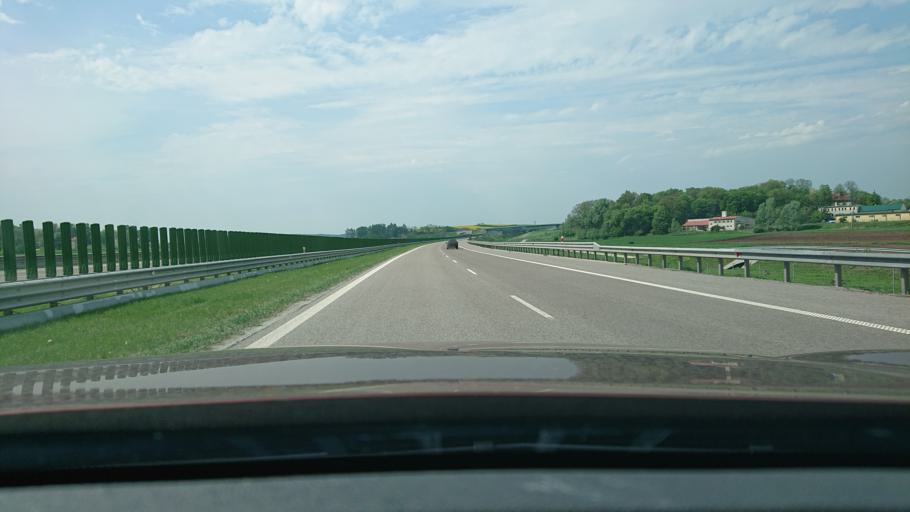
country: PL
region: Subcarpathian Voivodeship
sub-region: Powiat jaroslawski
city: Rokietnica
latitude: 49.9391
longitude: 22.6775
